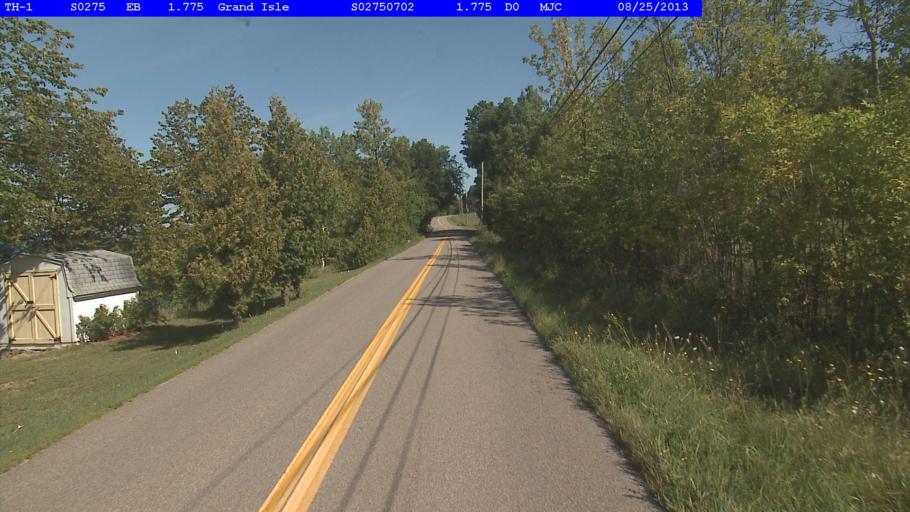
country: US
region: New York
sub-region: Clinton County
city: Cumberland Head
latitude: 44.7254
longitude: -73.3380
